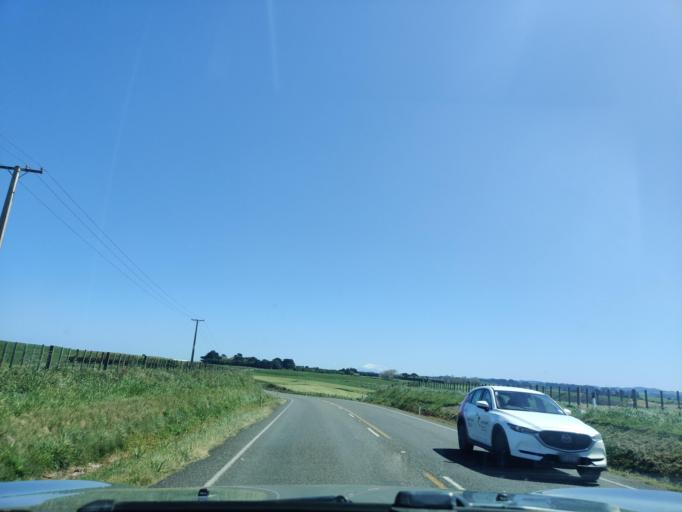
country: NZ
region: Taranaki
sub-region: South Taranaki District
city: Patea
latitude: -39.7981
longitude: 174.7139
